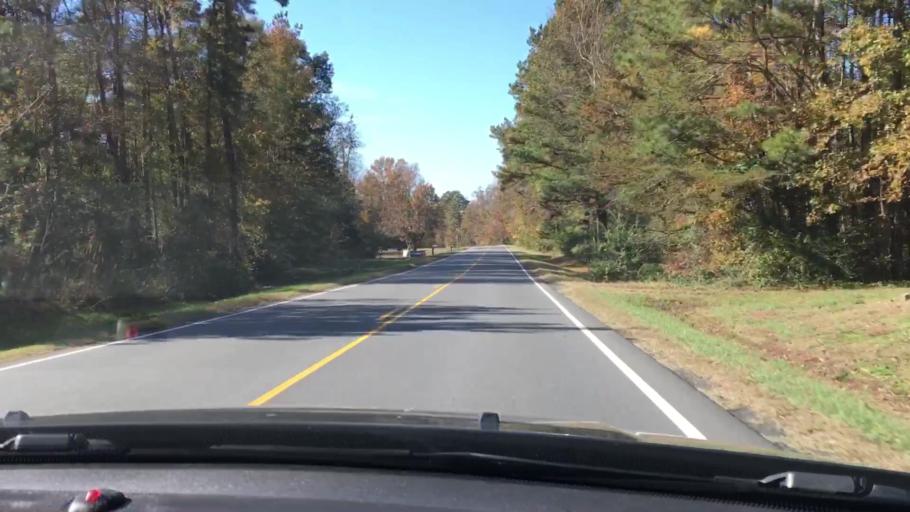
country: US
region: Virginia
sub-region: King William County
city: King William
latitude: 37.6744
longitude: -76.9814
